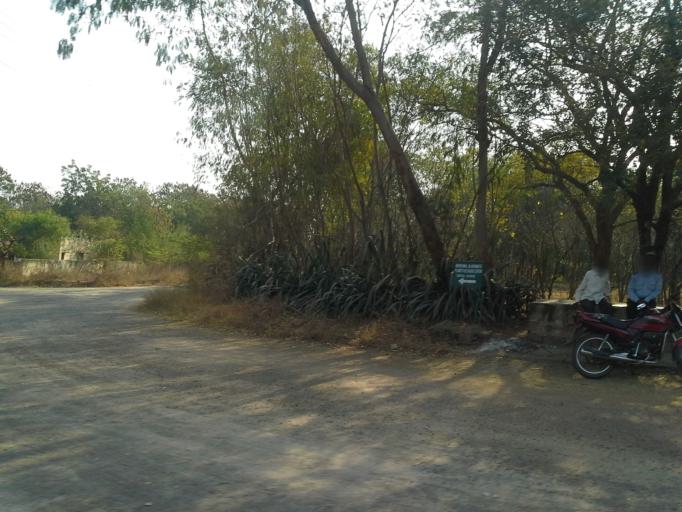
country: IN
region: Telangana
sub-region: Hyderabad
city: Hyderabad
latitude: 17.3148
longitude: 78.4208
